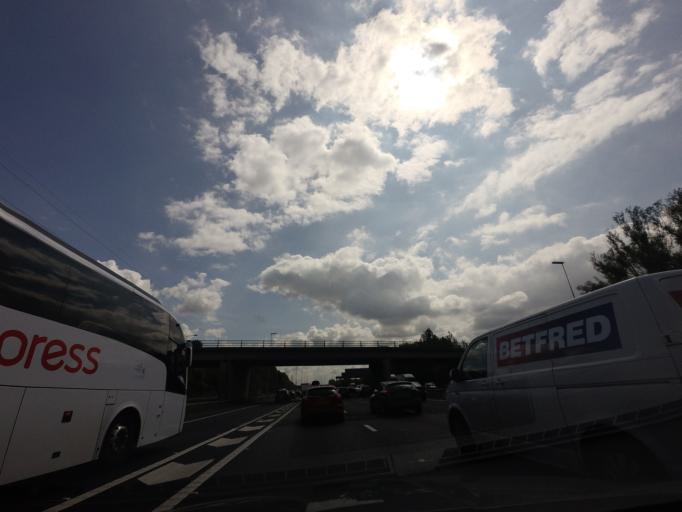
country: GB
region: England
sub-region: Warrington
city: Croft
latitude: 53.4186
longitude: -2.5449
